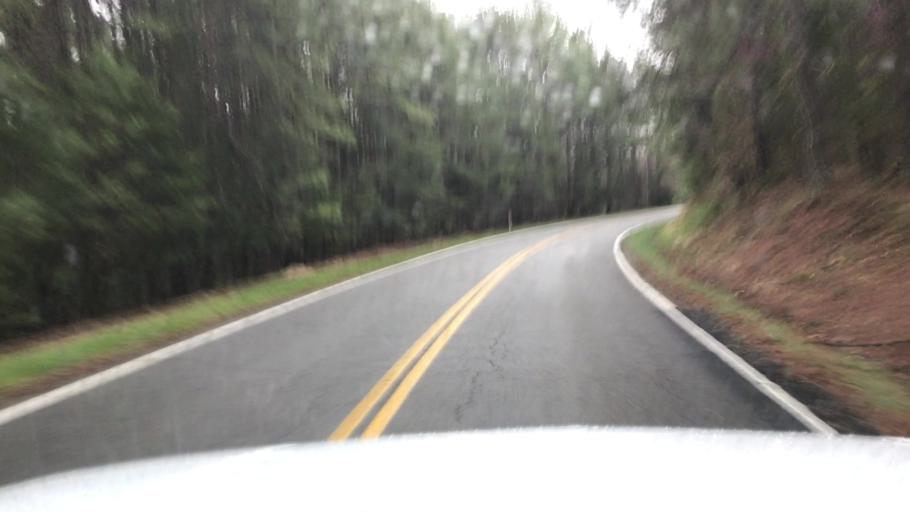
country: US
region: Virginia
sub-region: Henrico County
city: Short Pump
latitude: 37.6343
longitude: -77.6792
